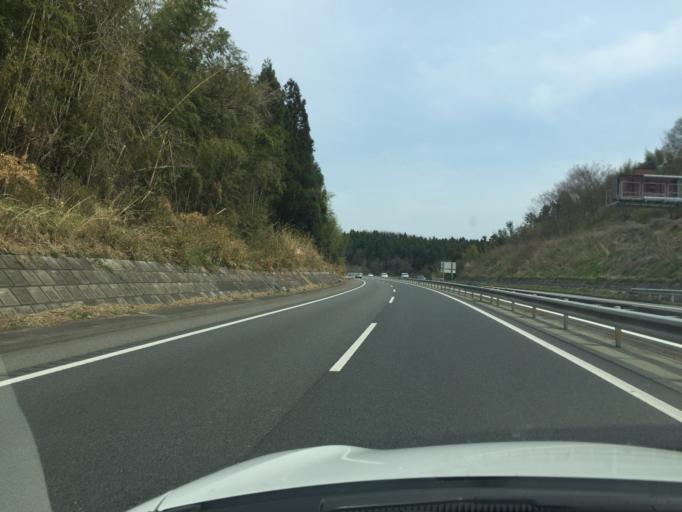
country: JP
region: Fukushima
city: Miharu
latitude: 37.4400
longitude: 140.4447
